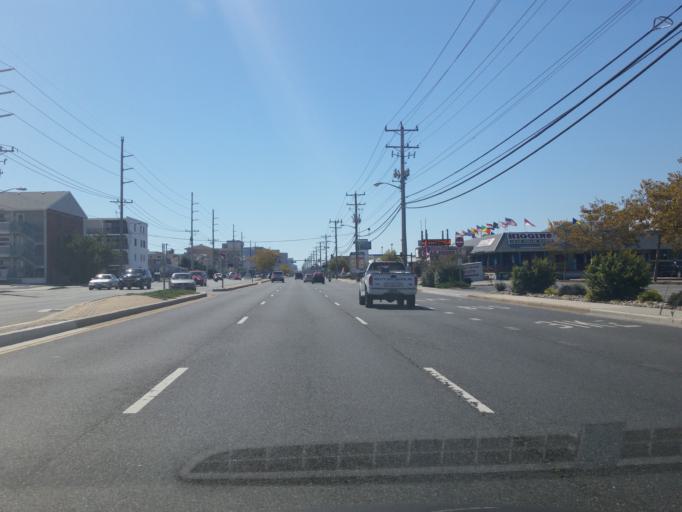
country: US
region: Maryland
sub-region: Worcester County
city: Ocean City
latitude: 38.4345
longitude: -75.0546
